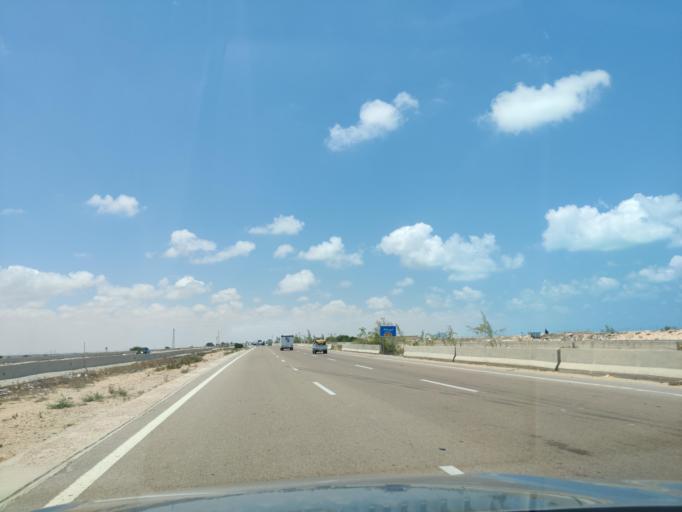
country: EG
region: Muhafazat Matruh
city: Al `Alamayn
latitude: 30.8124
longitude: 29.0824
